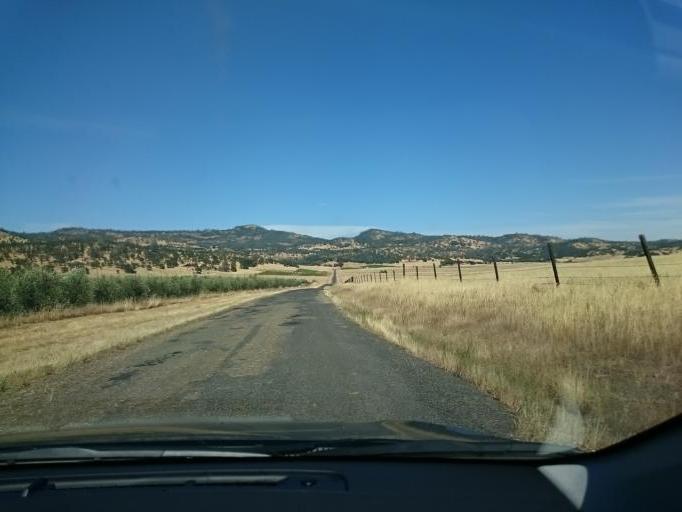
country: US
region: California
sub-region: Calaveras County
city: Copperopolis
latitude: 38.0491
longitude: -120.7147
